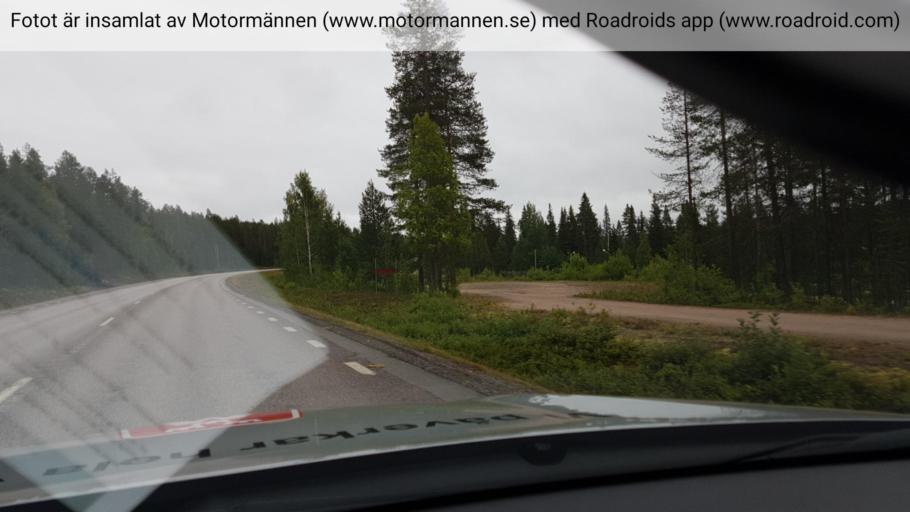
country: SE
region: Norrbotten
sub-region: Gallivare Kommun
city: Gaellivare
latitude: 67.1349
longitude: 20.7306
